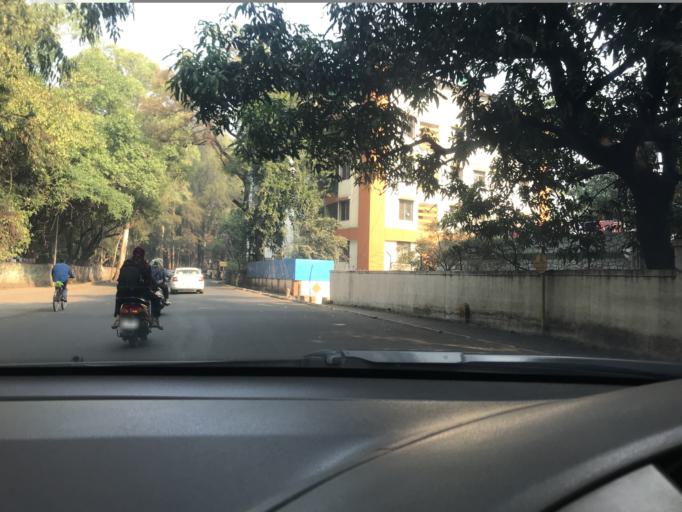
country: IN
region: Maharashtra
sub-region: Pune Division
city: Pune
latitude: 18.5085
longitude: 73.8287
